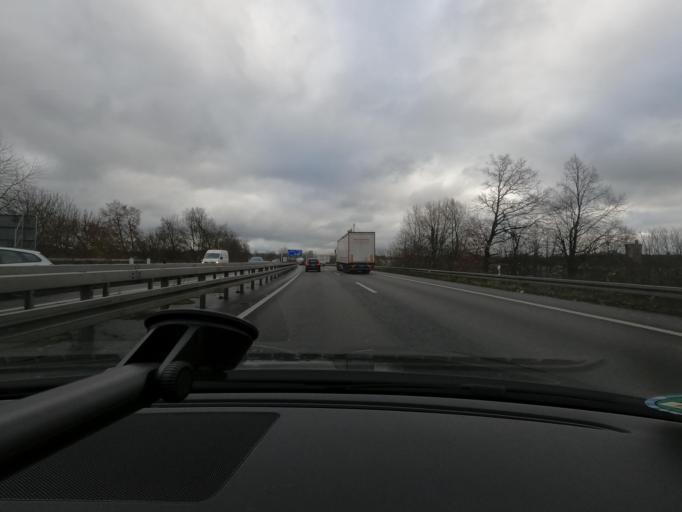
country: DE
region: North Rhine-Westphalia
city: Witten
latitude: 51.4932
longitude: 7.3567
